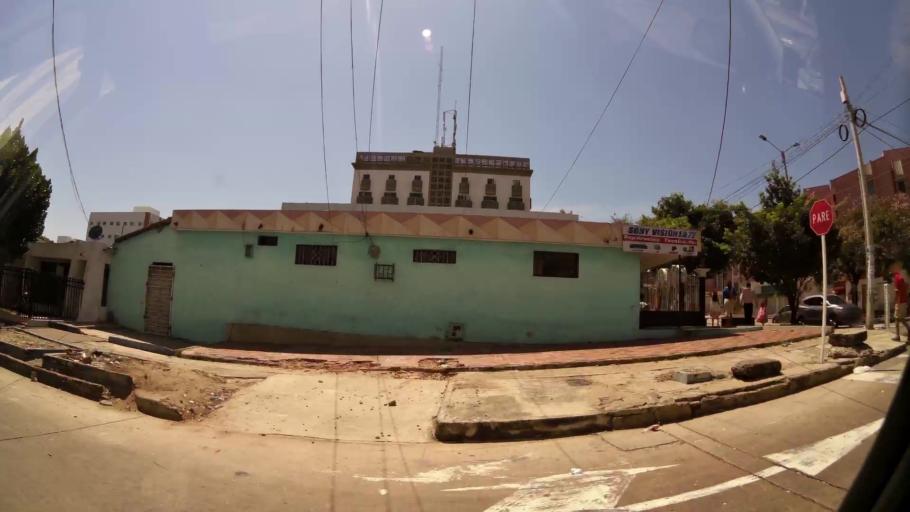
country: CO
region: Atlantico
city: Barranquilla
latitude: 10.9872
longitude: -74.8094
